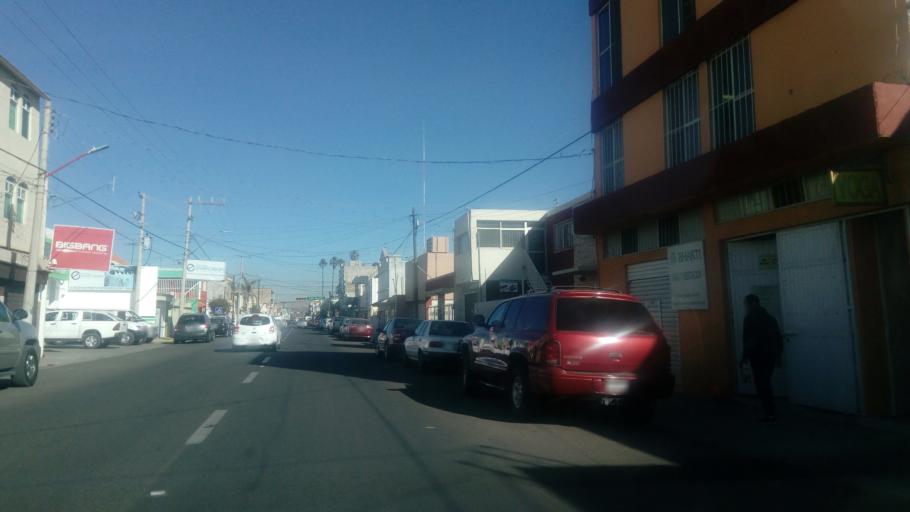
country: MX
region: Durango
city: Victoria de Durango
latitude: 24.0230
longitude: -104.6572
